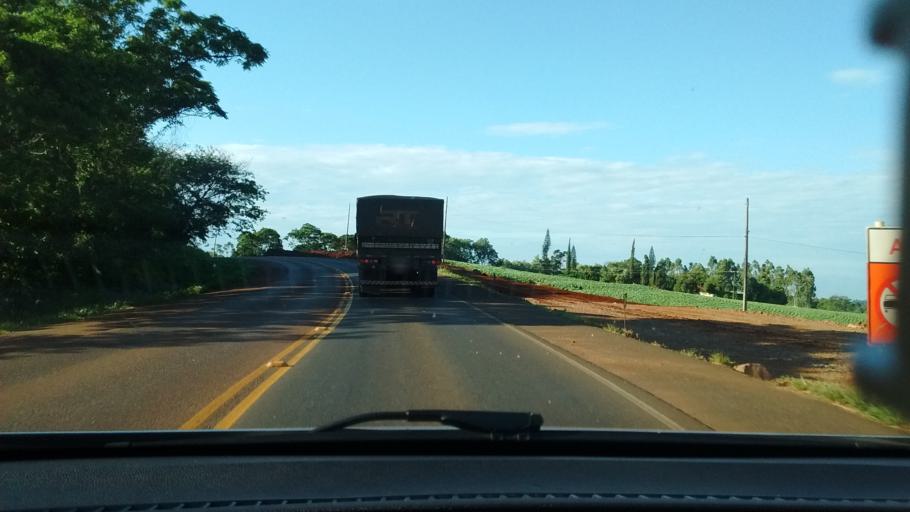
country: BR
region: Parana
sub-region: Cascavel
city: Cascavel
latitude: -25.2072
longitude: -53.5975
